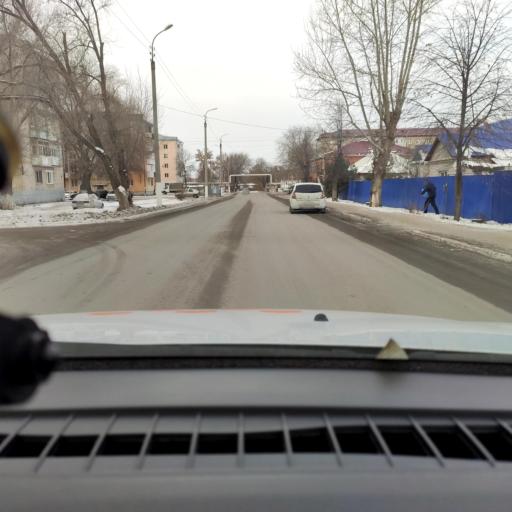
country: RU
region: Samara
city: Chapayevsk
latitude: 52.9599
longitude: 49.6881
